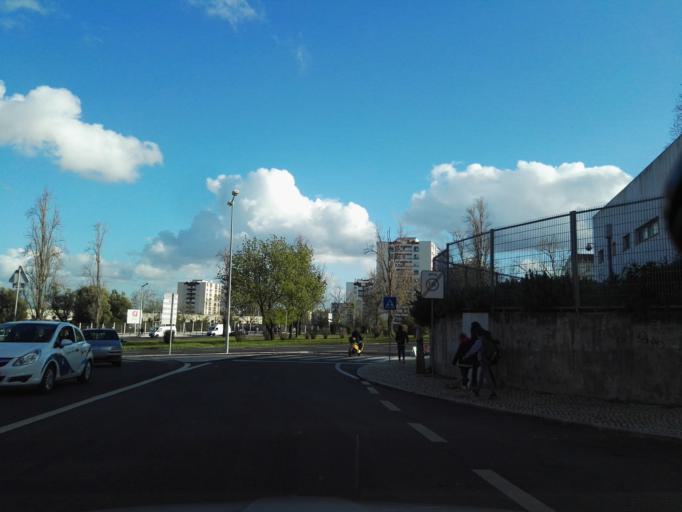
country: PT
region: Lisbon
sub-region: Loures
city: Moscavide
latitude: 38.7714
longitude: -9.1097
